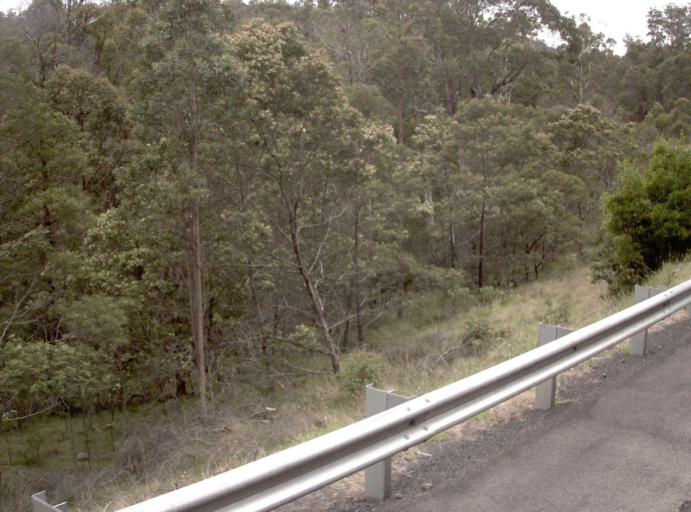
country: AU
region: New South Wales
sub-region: Bombala
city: Bombala
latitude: -37.2573
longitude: 149.2411
